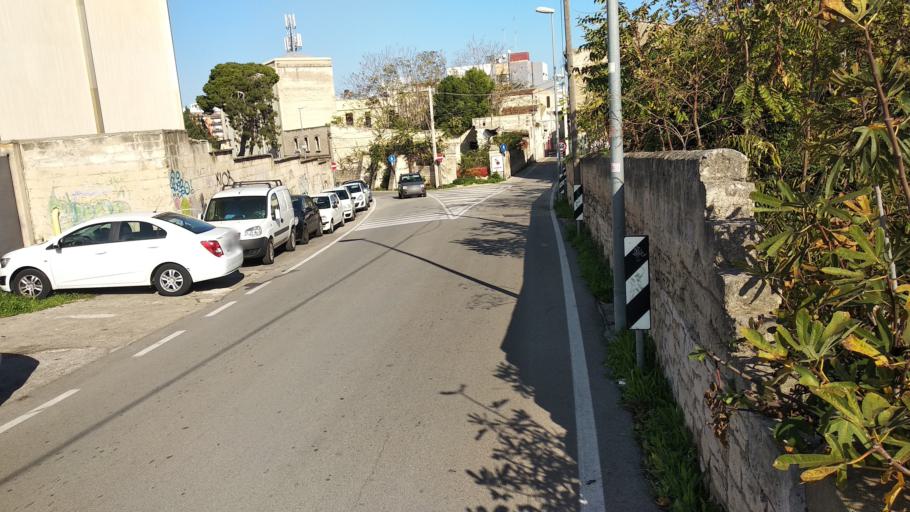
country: IT
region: Apulia
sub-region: Provincia di Bari
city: Bari
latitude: 41.1148
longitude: 16.8573
